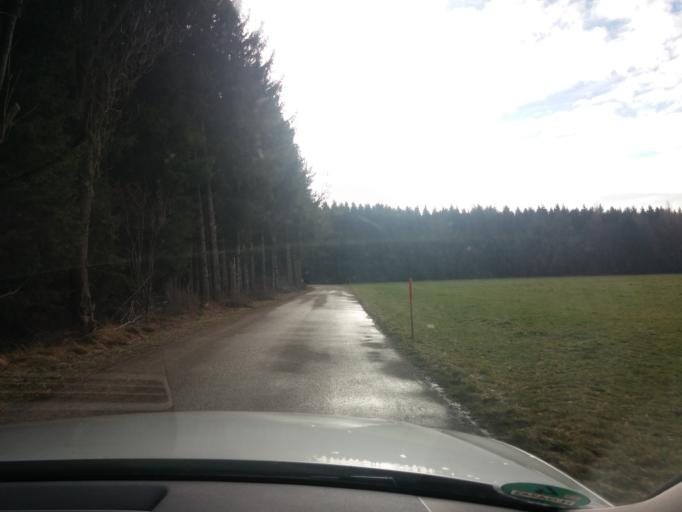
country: DE
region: Bavaria
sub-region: Swabia
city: Kronburg
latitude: 47.8827
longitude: 10.1486
